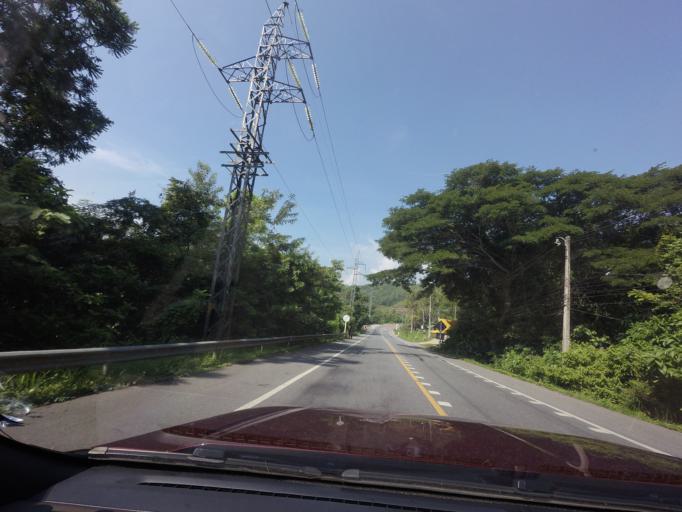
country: TH
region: Yala
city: Than To
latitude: 5.9611
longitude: 101.1946
